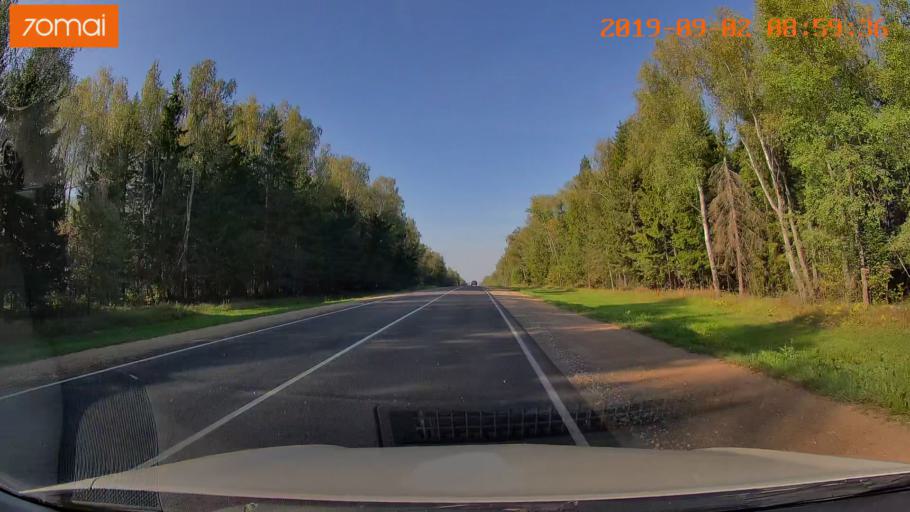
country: RU
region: Kaluga
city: Myatlevo
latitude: 54.9198
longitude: 35.7274
